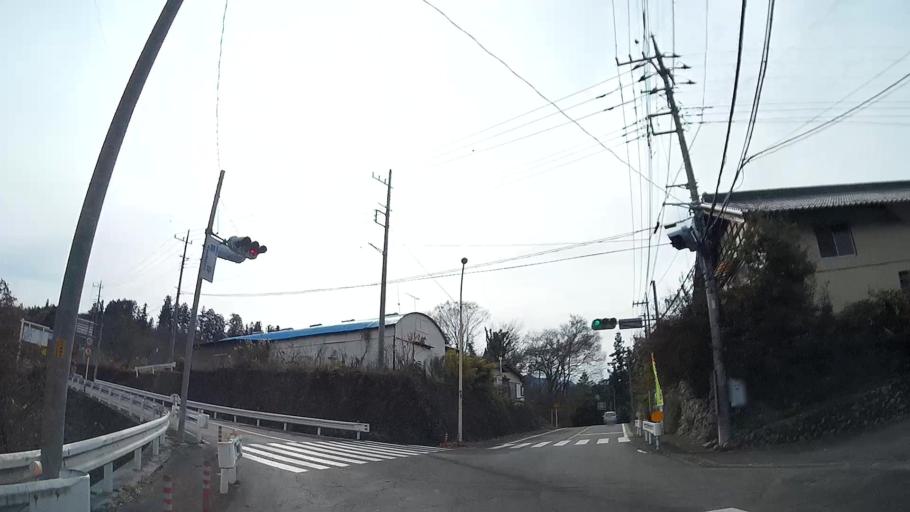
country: JP
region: Saitama
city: Chichibu
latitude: 35.9869
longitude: 139.0330
